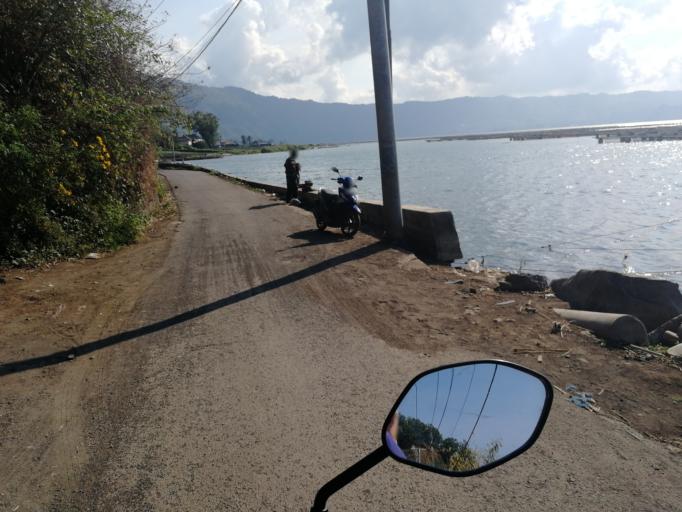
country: ID
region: Bali
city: Banjar Trunyan
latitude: -8.2614
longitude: 115.4225
